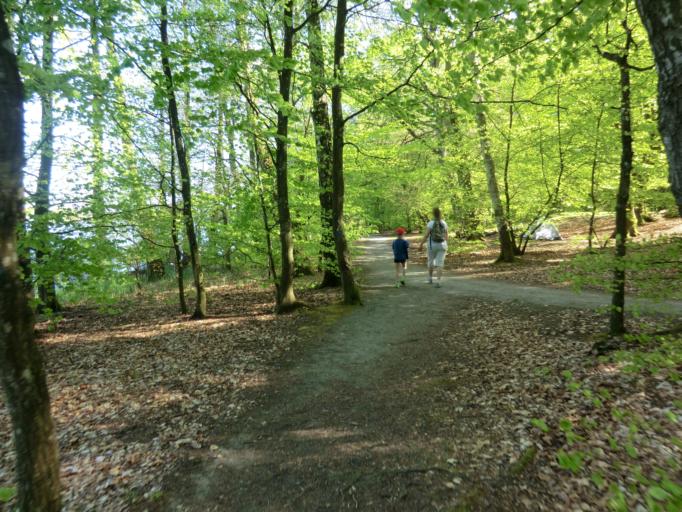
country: SE
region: Skane
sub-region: Sjobo Kommun
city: Sjoebo
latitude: 55.5693
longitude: 13.7187
